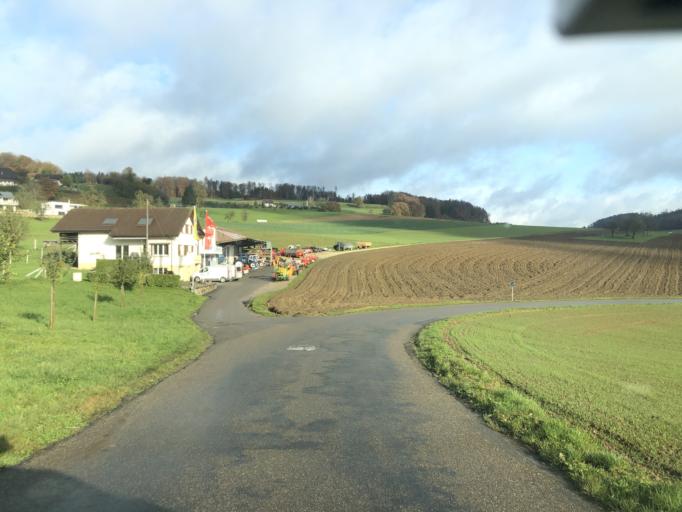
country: CH
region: Aargau
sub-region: Bezirk Baden
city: Unterehrendingen
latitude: 47.5203
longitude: 8.3632
